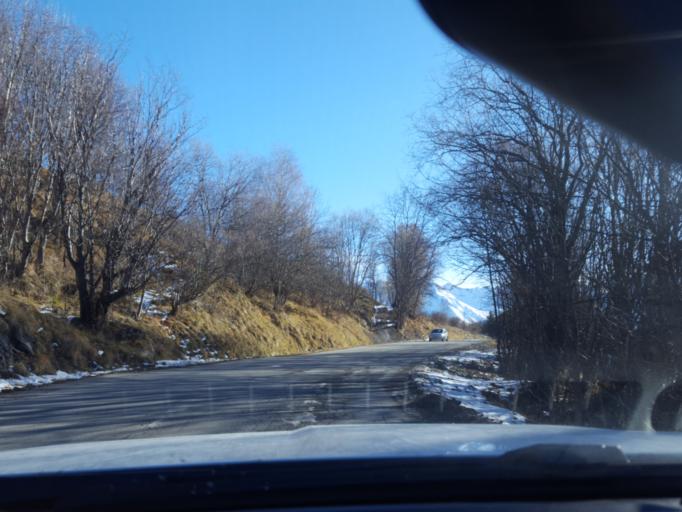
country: FR
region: Rhone-Alpes
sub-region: Departement de la Savoie
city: Saint-Jean-de-Maurienne
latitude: 45.2151
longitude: 6.2535
